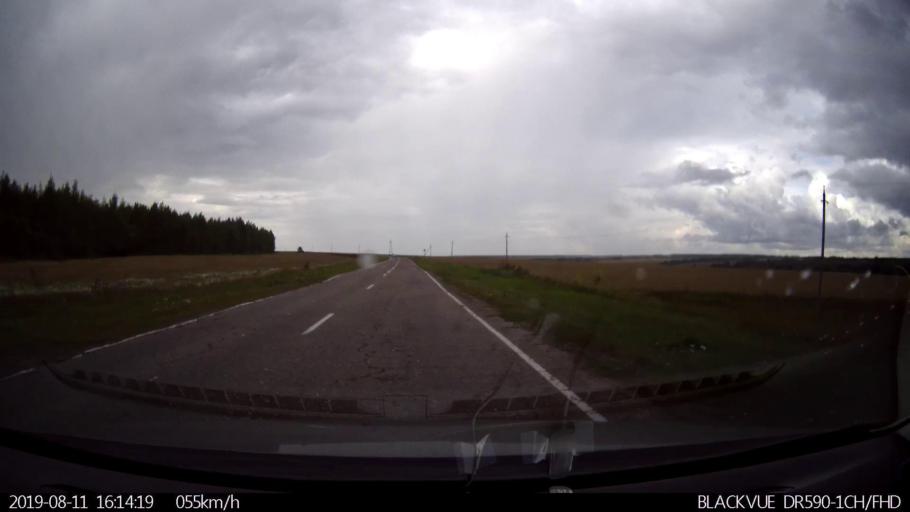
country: RU
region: Ulyanovsk
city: Ignatovka
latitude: 54.0271
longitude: 47.6343
